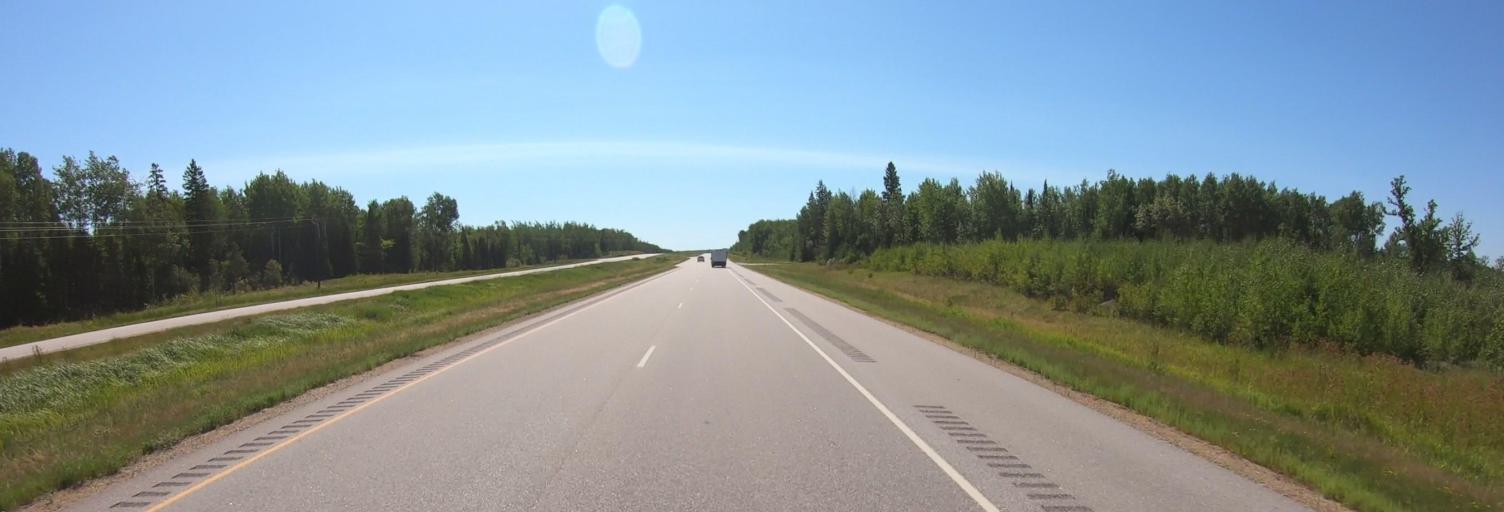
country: US
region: Minnesota
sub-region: Saint Louis County
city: Mountain Iron
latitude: 47.7954
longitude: -92.6672
